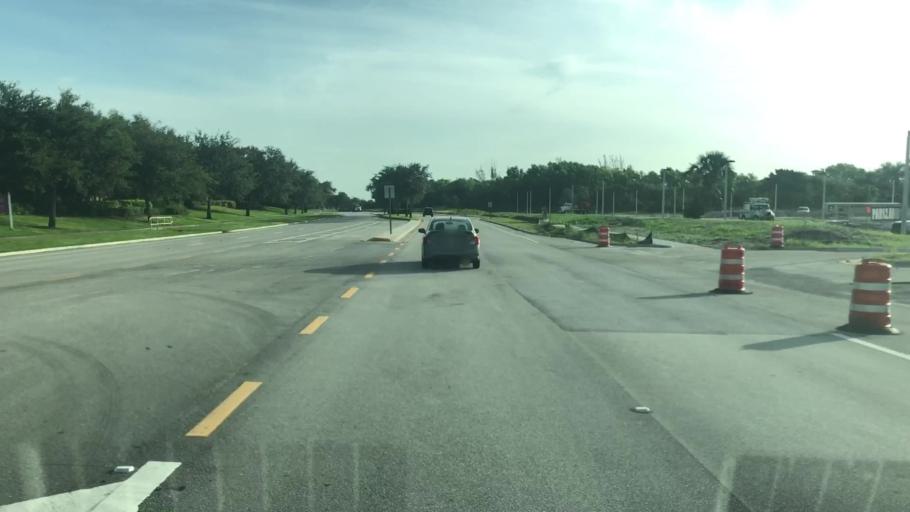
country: US
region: Florida
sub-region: Broward County
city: Parkland
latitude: 26.3141
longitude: -80.2522
